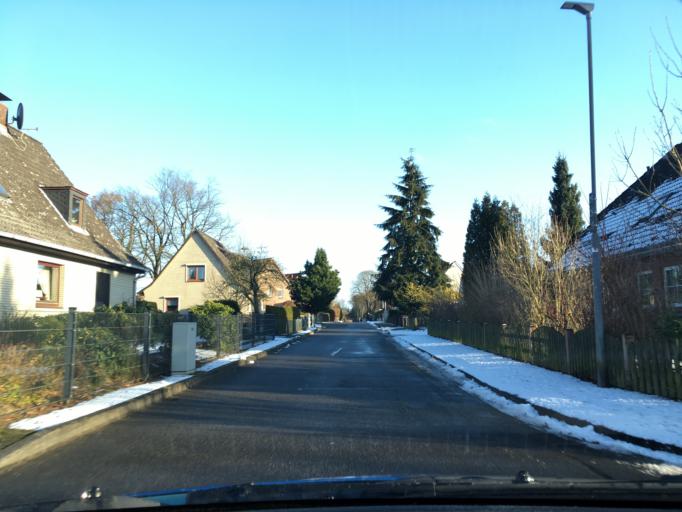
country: DE
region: Schleswig-Holstein
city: Buchen
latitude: 53.4854
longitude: 10.5955
